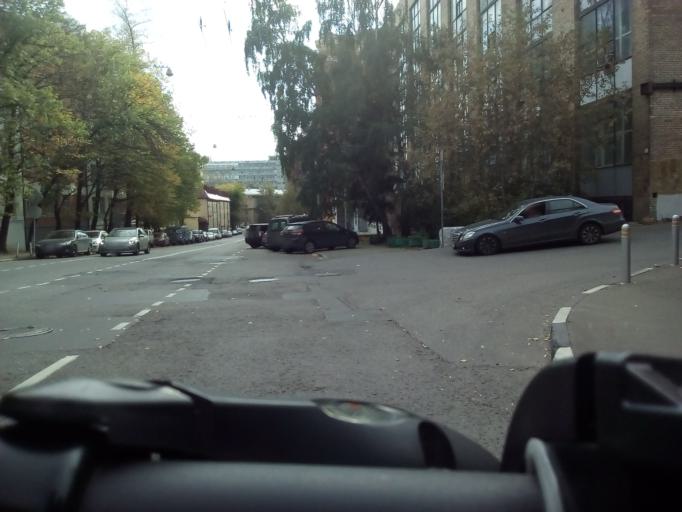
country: RU
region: Moscow
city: Lefortovo
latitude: 55.7897
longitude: 37.7070
